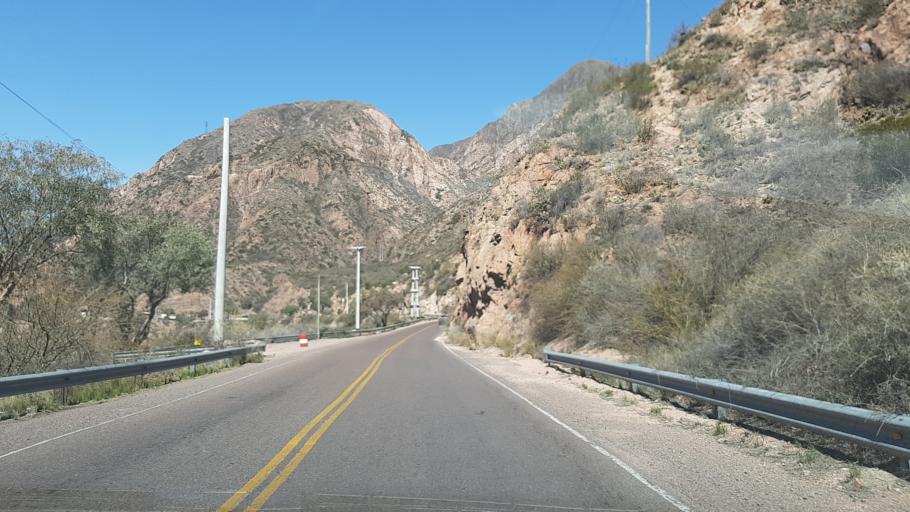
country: AR
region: Mendoza
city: Lujan de Cuyo
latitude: -33.0251
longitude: -69.1167
